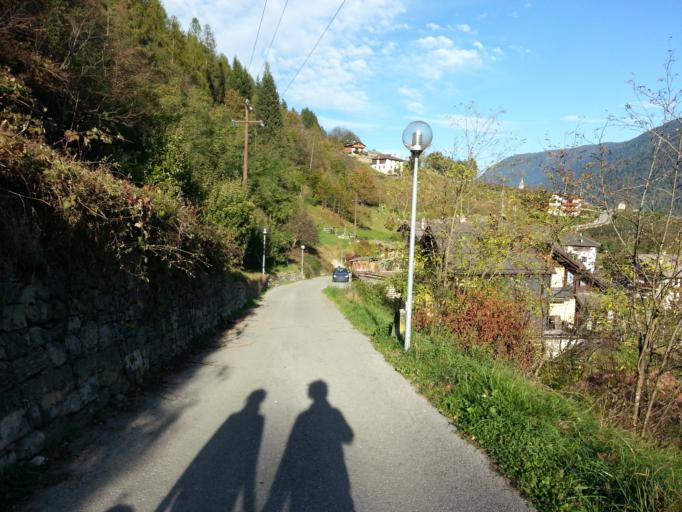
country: IT
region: Trentino-Alto Adige
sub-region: Provincia di Trento
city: Monclassico
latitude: 46.3336
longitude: 10.8787
